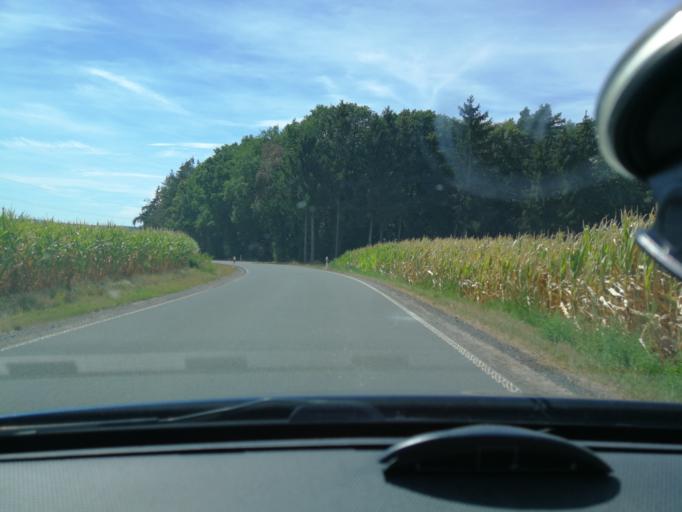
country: DE
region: Rheinland-Pfalz
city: Heidweiler
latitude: 49.9205
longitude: 6.7627
